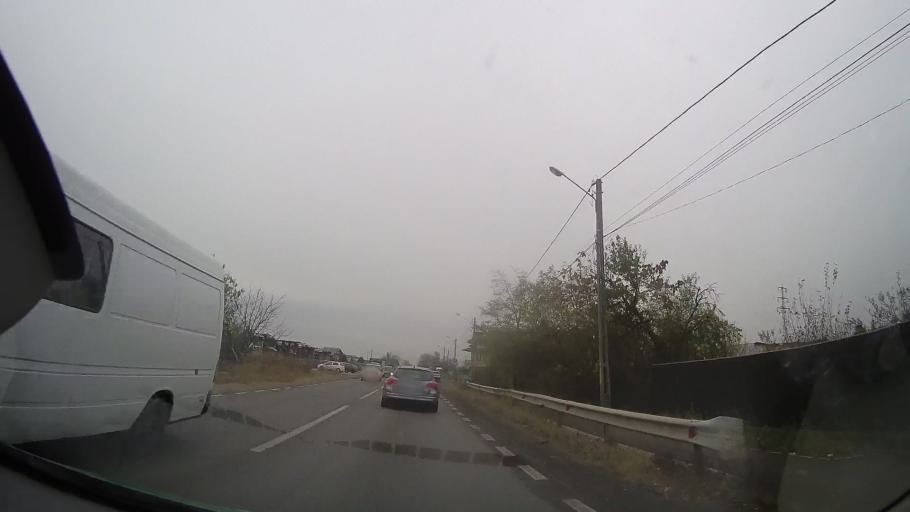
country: RO
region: Prahova
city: Ploiesti
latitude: 44.9632
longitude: 26.0361
